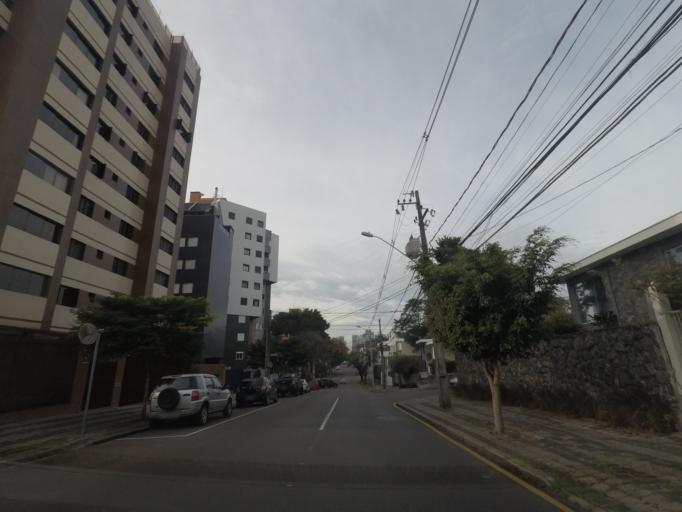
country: BR
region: Parana
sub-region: Curitiba
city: Curitiba
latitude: -25.4356
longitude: -49.2931
